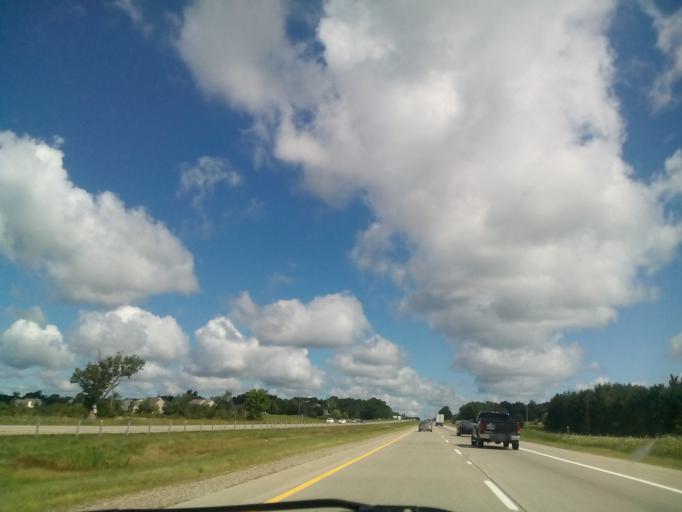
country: US
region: Michigan
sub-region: Genesee County
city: Fenton
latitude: 42.7126
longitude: -83.7622
